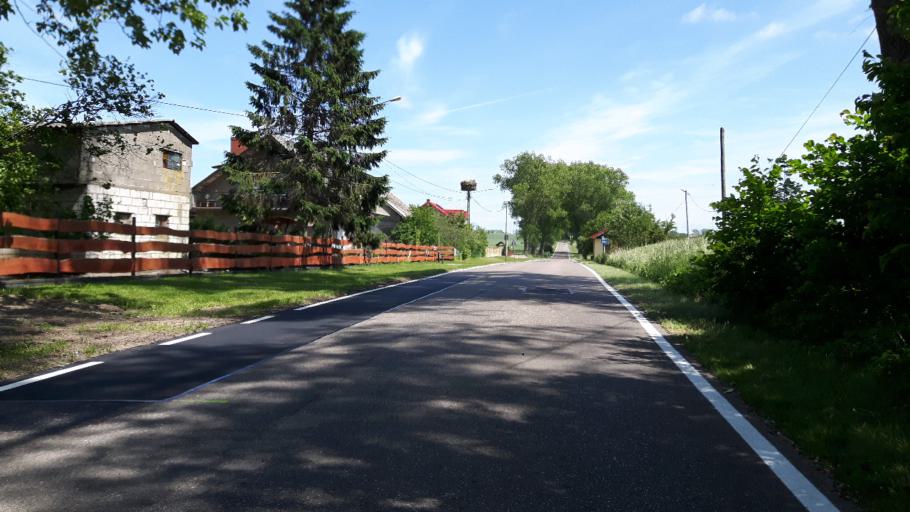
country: PL
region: Pomeranian Voivodeship
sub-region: Powiat wejherowski
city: Gniewino
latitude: 54.7207
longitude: 17.9867
